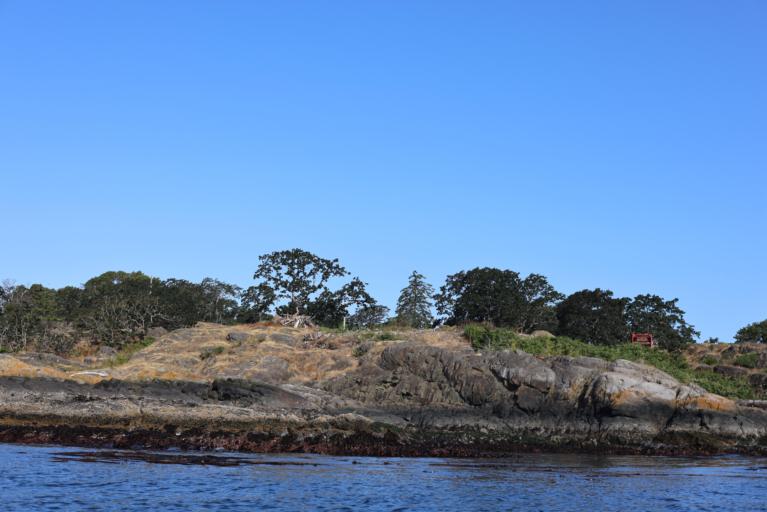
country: CA
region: British Columbia
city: Metchosin
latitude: 48.3437
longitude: -123.5299
